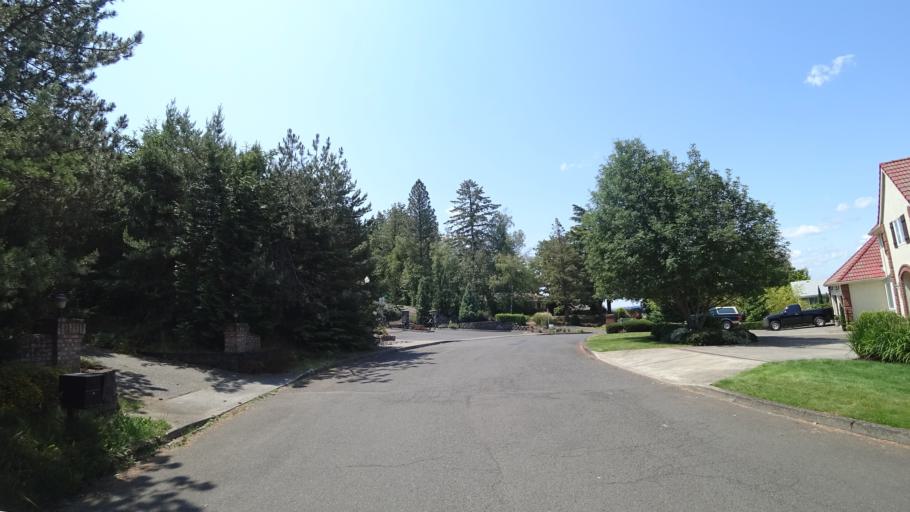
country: US
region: Oregon
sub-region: Multnomah County
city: Lents
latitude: 45.4614
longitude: -122.5630
